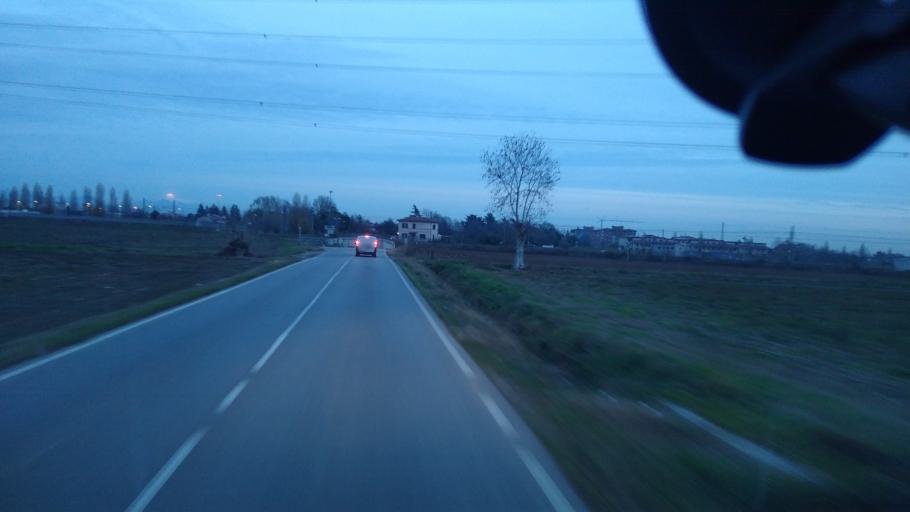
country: IT
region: Lombardy
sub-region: Provincia di Bergamo
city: Arcene
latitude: 45.5730
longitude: 9.6021
